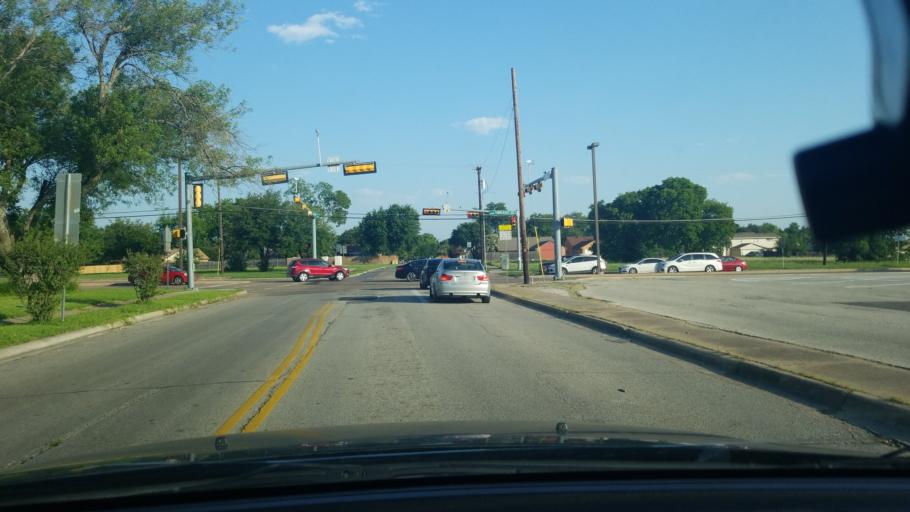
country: US
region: Texas
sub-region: Dallas County
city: Mesquite
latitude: 32.8043
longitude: -96.6420
